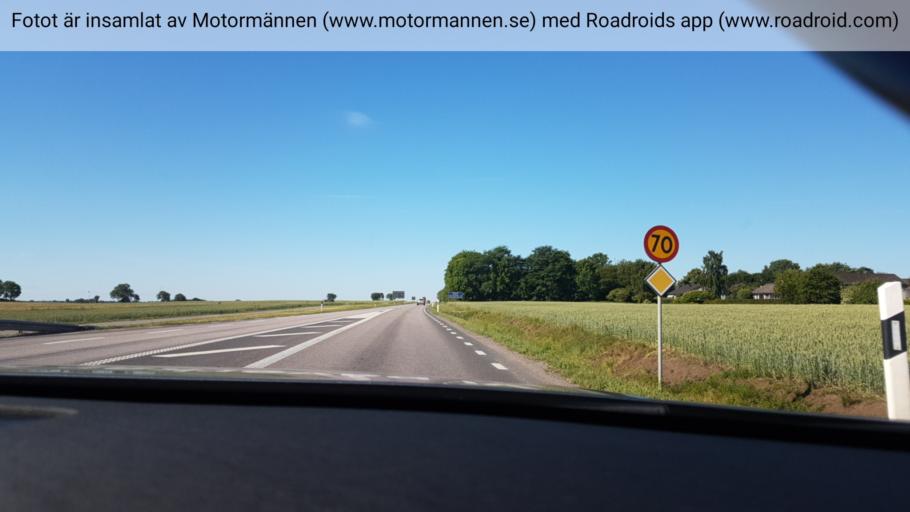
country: SE
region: Vaestra Goetaland
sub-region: Falkopings Kommun
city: Falkoeping
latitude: 58.1583
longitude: 13.5714
